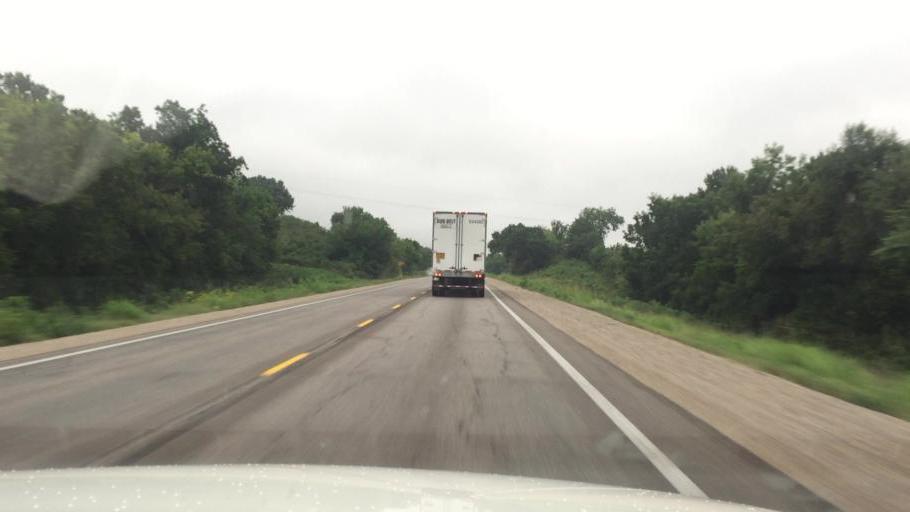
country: US
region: Kansas
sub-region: Montgomery County
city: Cherryvale
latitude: 37.1628
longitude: -95.5767
